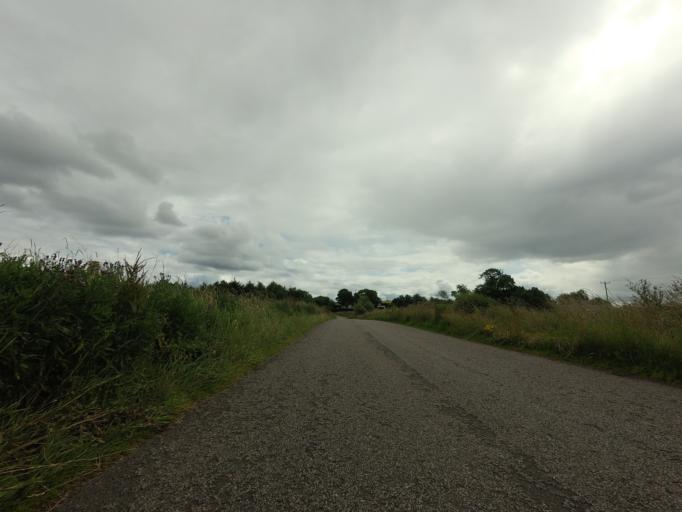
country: GB
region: Scotland
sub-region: Moray
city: Lhanbryd
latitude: 57.6582
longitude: -3.2026
